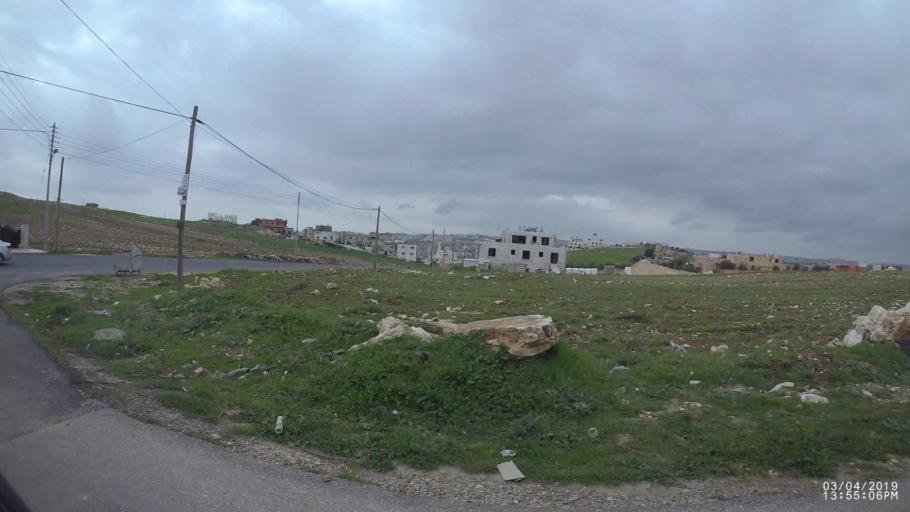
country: JO
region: Amman
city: Wadi as Sir
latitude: 31.9291
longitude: 35.8551
